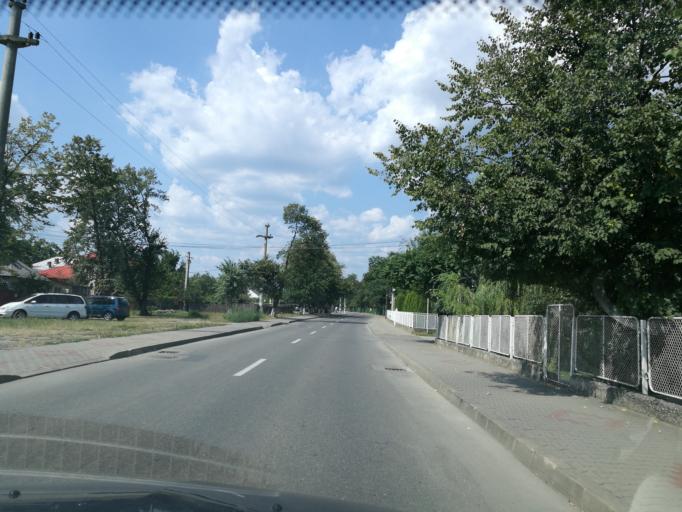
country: RO
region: Neamt
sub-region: Oras Targu Neamt
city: Humulesti
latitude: 47.2089
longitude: 26.3491
